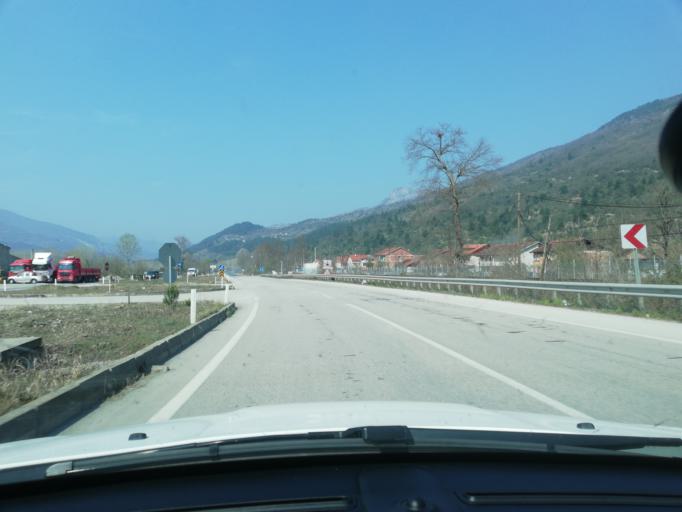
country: TR
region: Karabuk
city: Yenice
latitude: 41.2166
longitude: 32.3047
